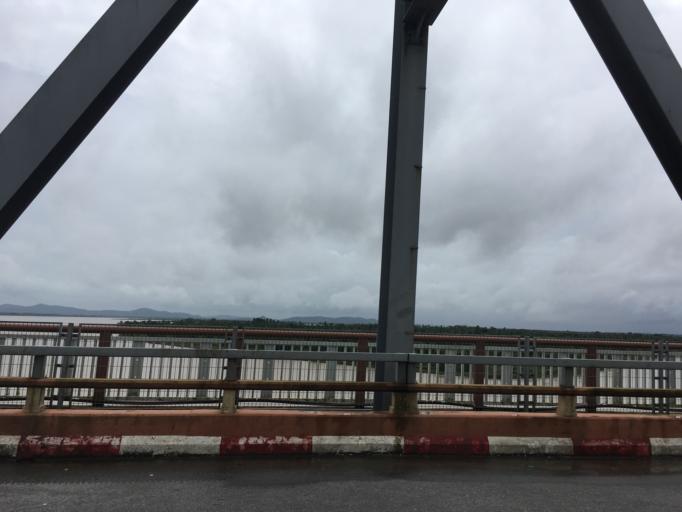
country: MM
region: Mon
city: Martaban
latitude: 16.5165
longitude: 97.6154
